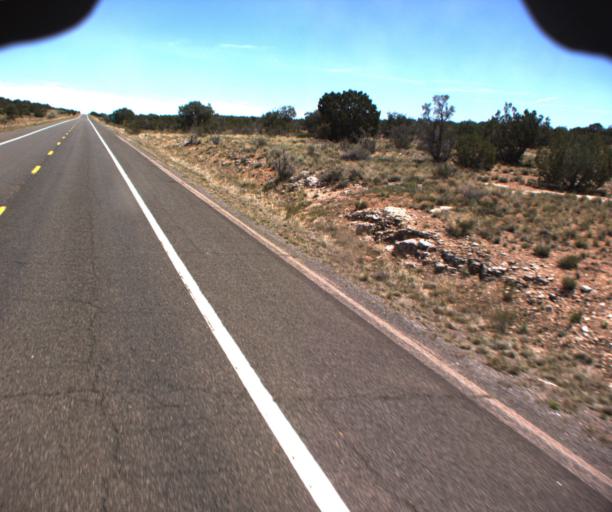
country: US
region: Arizona
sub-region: Mohave County
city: Peach Springs
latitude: 35.5509
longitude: -113.3082
